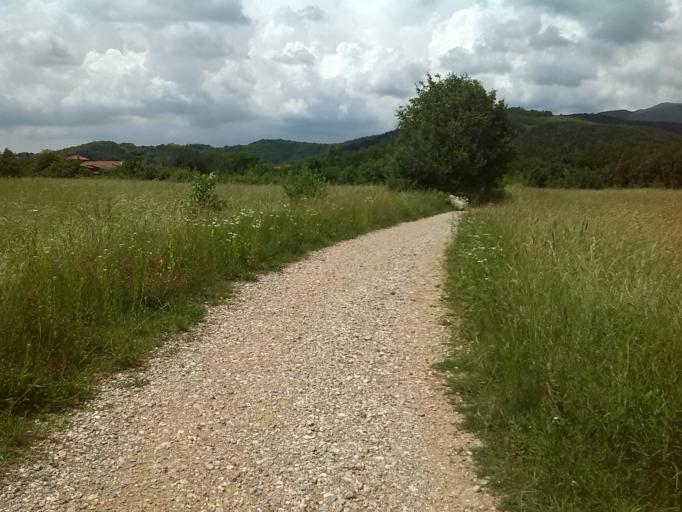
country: IT
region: Friuli Venezia Giulia
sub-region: Provincia di Udine
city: Cividale del Friuli
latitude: 46.0979
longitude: 13.4513
